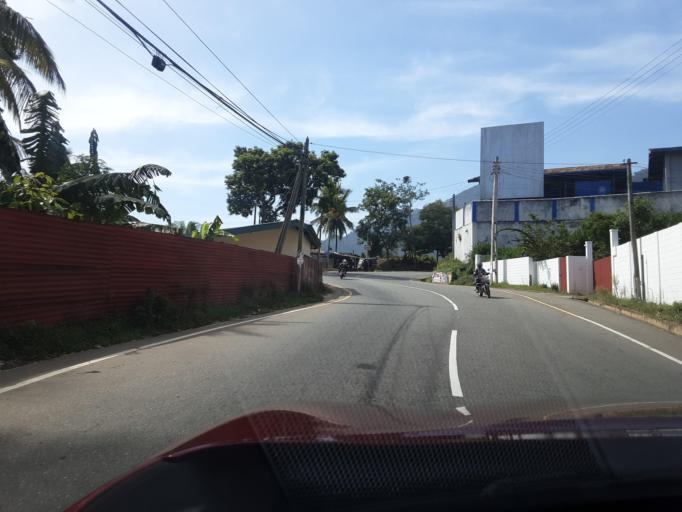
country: LK
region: Uva
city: Badulla
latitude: 6.9778
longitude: 81.0854
